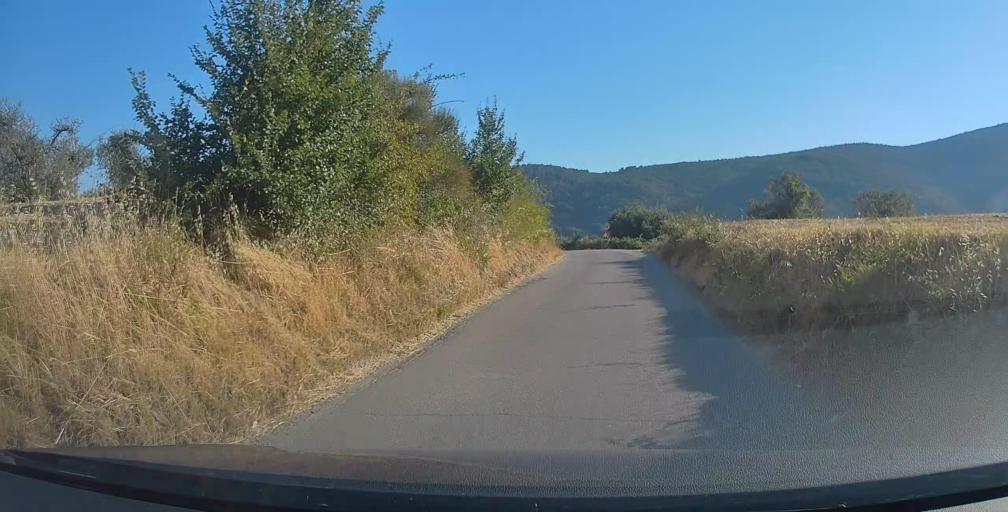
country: IT
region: Umbria
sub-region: Provincia di Terni
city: Calvi dell'Umbria
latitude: 42.3836
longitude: 12.5686
